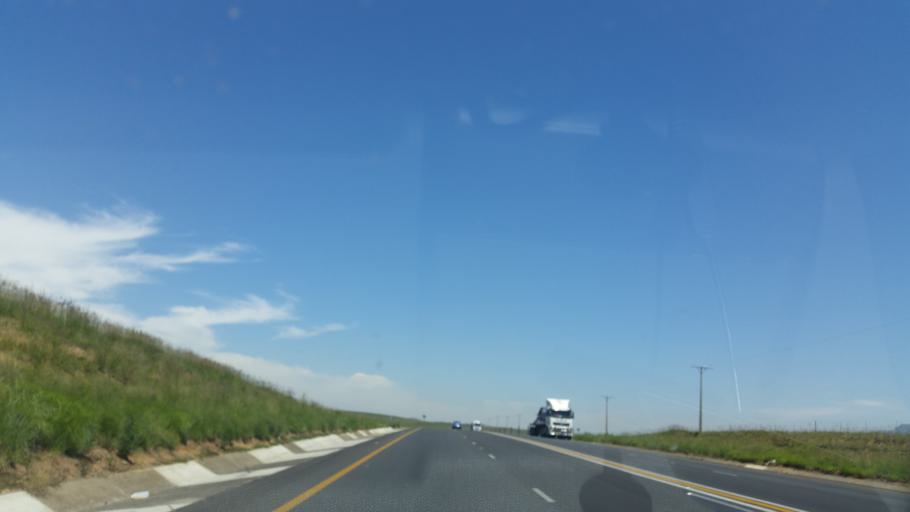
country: ZA
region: Orange Free State
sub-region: Thabo Mofutsanyana District Municipality
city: Harrismith
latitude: -28.3665
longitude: 29.3468
